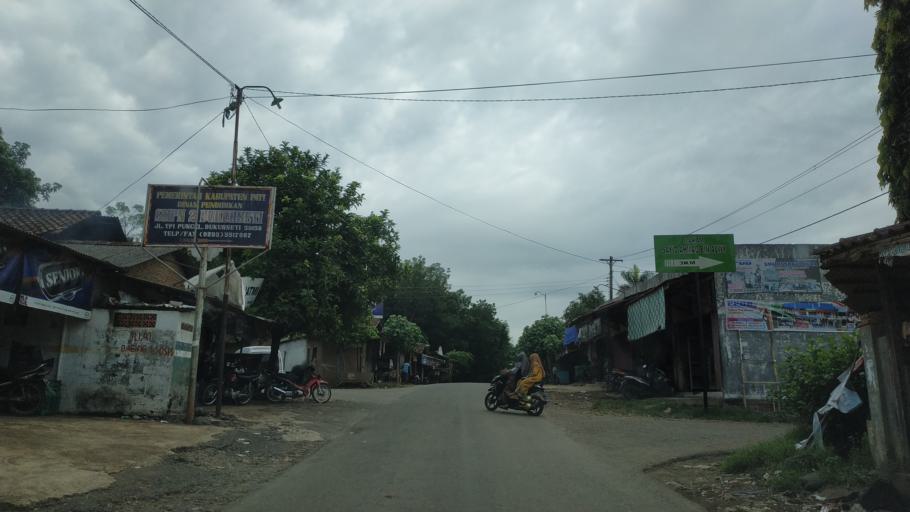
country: ID
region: Central Java
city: Krajan Tegalombo
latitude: -6.4423
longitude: 110.9823
